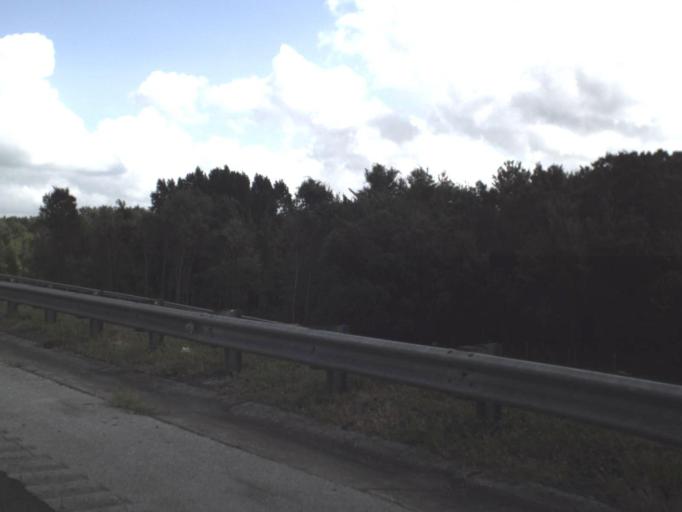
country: US
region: Florida
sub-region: Pasco County
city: San Antonio
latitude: 28.3256
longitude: -82.3244
